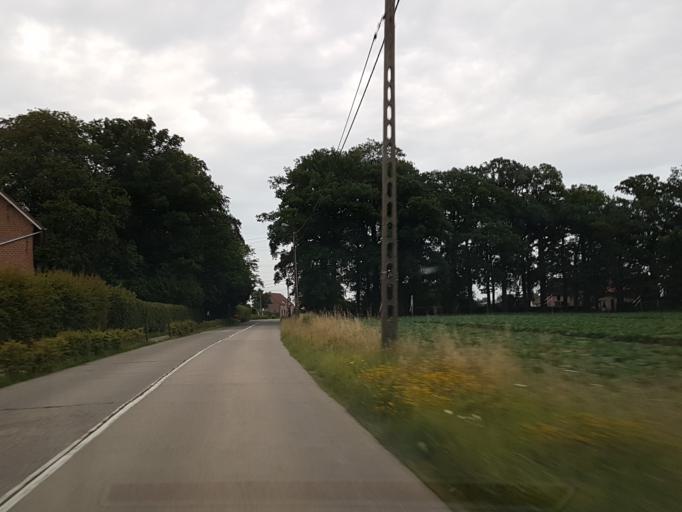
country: BE
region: Flanders
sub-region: Provincie Vlaams-Brabant
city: Kapelle-op-den-Bos
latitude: 51.0093
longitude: 4.4020
